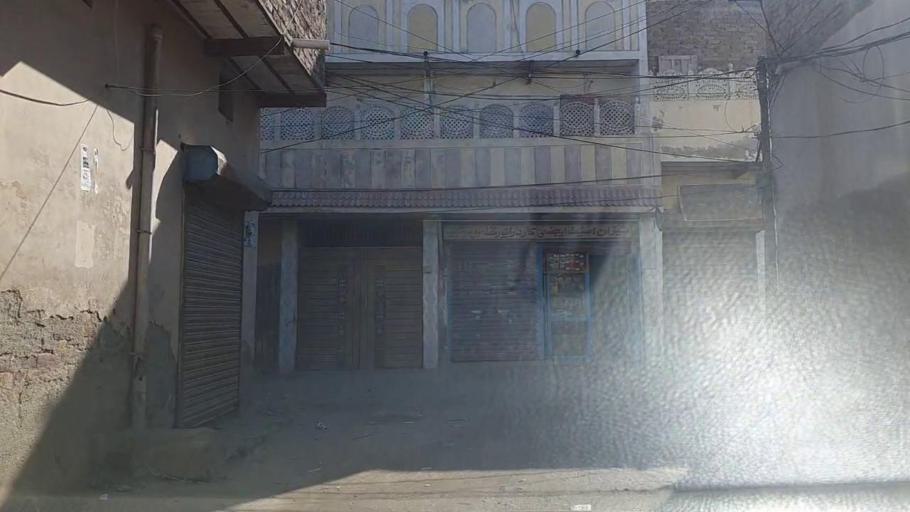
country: PK
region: Sindh
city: Nawabshah
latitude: 26.2549
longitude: 68.4242
